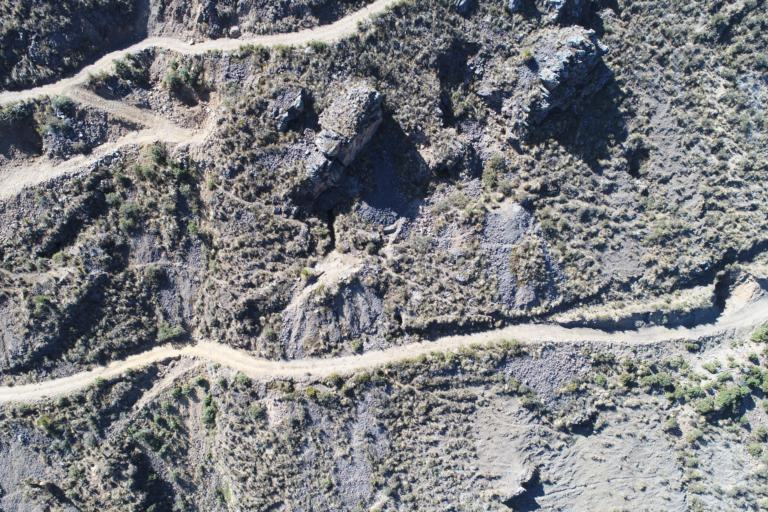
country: BO
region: La Paz
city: Viloco
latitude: -16.8127
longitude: -67.5528
